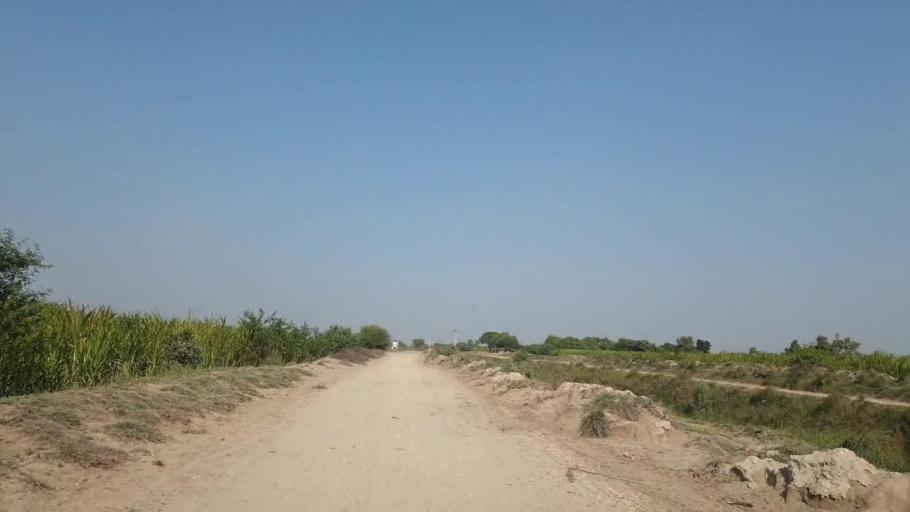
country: PK
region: Sindh
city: Bulri
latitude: 24.9297
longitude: 68.3804
